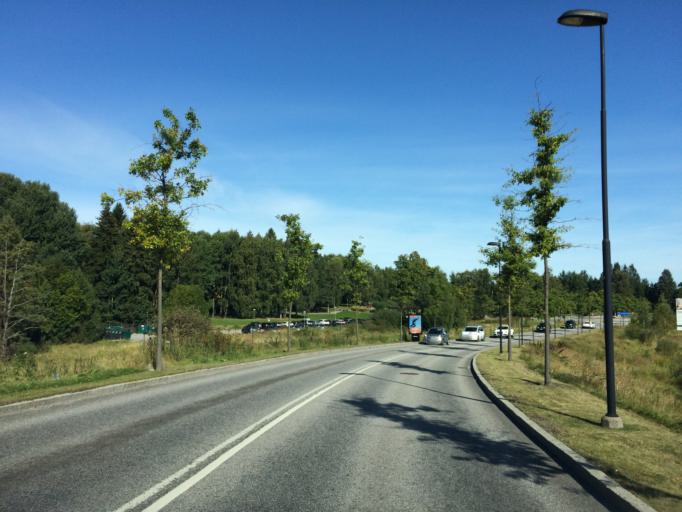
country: SE
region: Stockholm
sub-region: Stockholms Kommun
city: Kista
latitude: 59.4038
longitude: 17.9750
